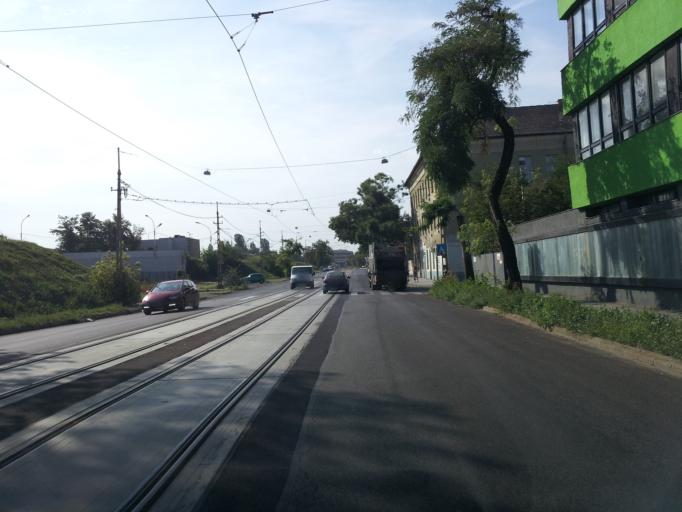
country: HU
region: Budapest
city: Budapest IX. keruelet
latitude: 47.4645
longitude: 19.0827
